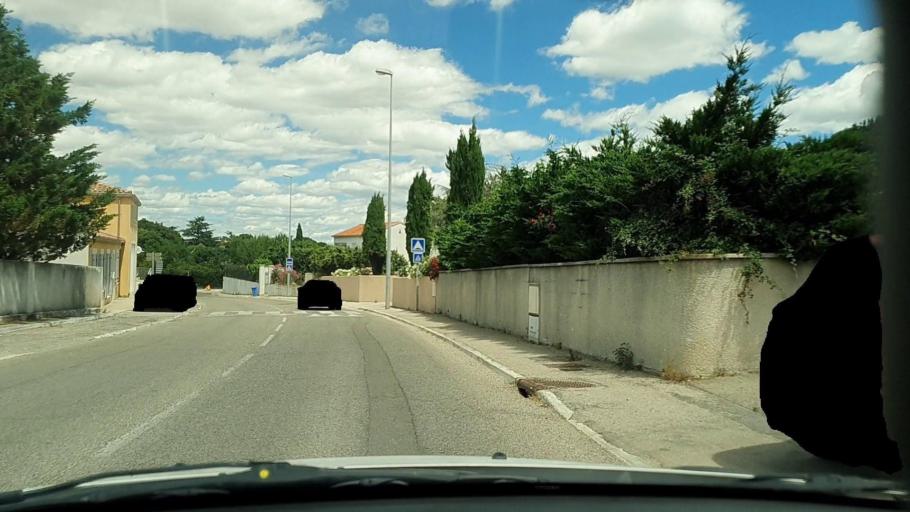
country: FR
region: Languedoc-Roussillon
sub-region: Departement du Gard
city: Poulx
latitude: 43.9077
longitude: 4.4213
